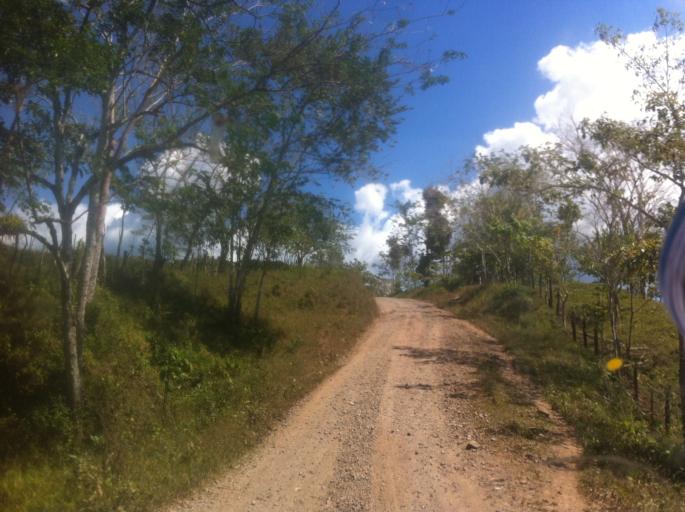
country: CR
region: Alajuela
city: Los Chiles
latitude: 11.2343
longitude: -84.5047
